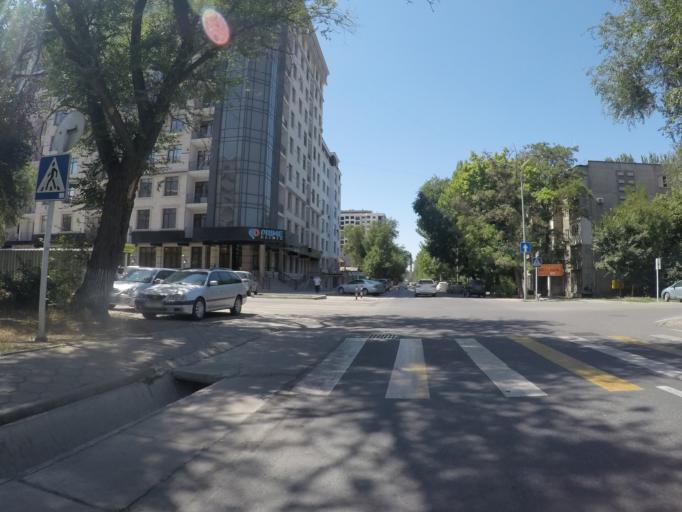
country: KG
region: Chuy
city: Bishkek
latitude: 42.8680
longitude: 74.5808
